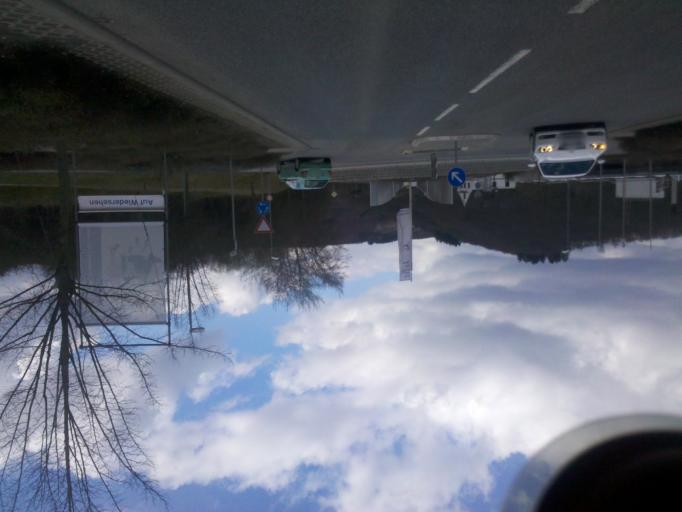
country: DE
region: Hesse
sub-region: Regierungsbezirk Giessen
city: Haiger
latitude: 50.7421
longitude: 8.2211
